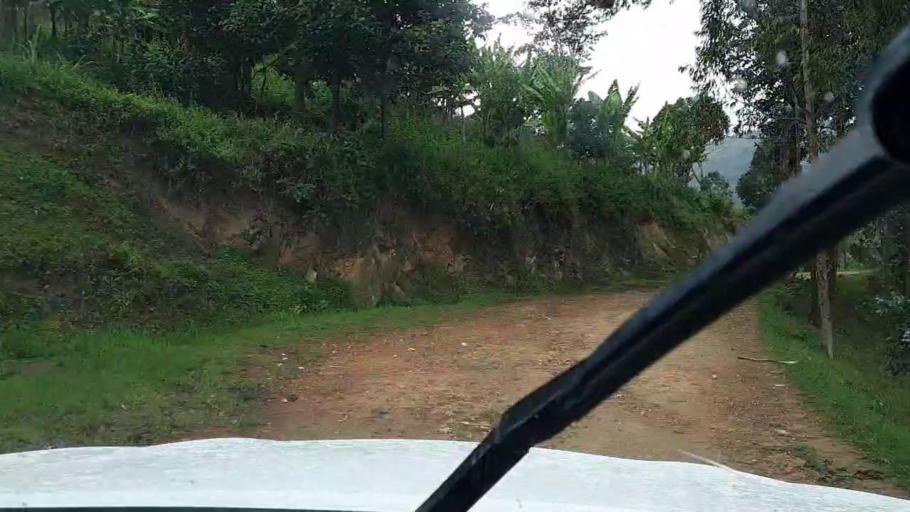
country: RW
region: Western Province
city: Kibuye
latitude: -2.0788
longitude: 29.4464
